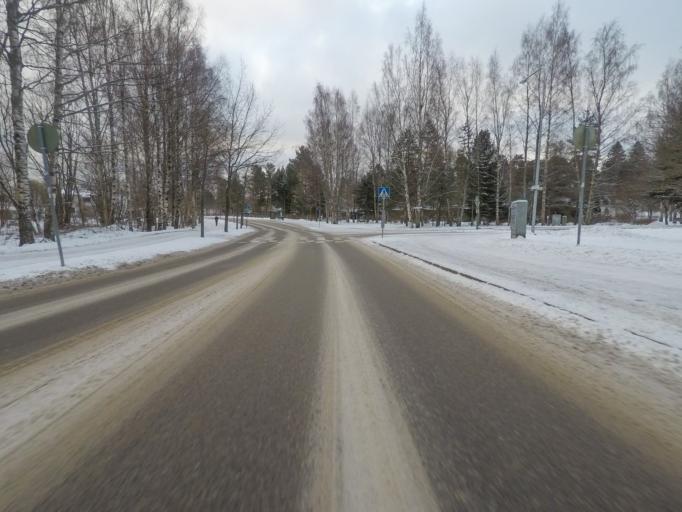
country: FI
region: Uusimaa
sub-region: Helsinki
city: Vantaa
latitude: 60.2143
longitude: 25.1470
